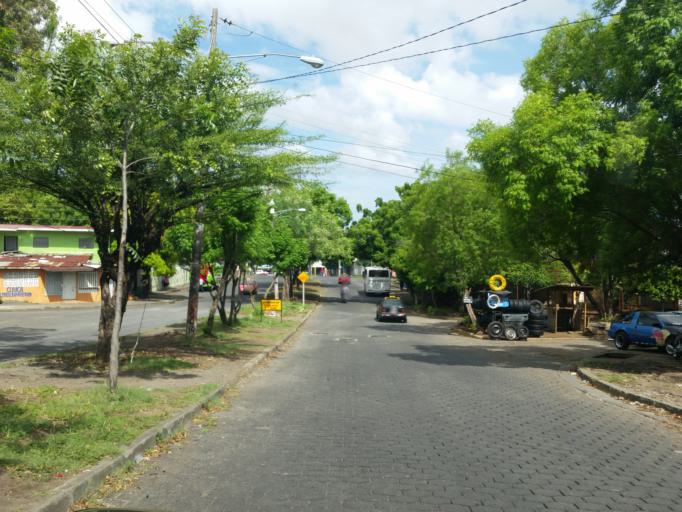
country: NI
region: Managua
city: Managua
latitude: 12.1338
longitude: -86.2374
